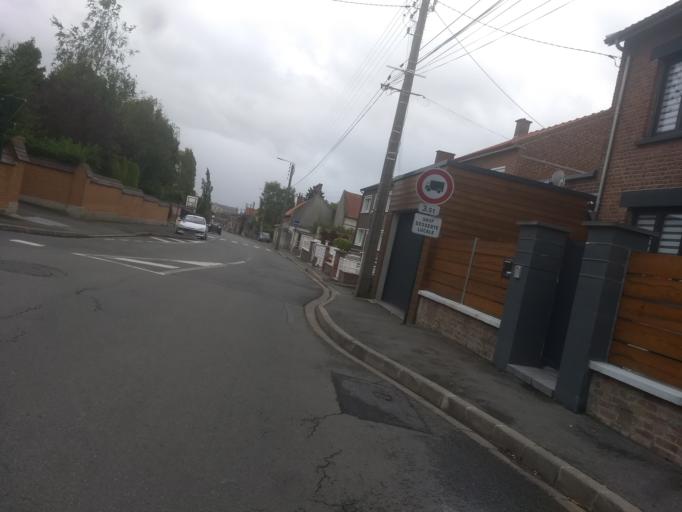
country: FR
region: Nord-Pas-de-Calais
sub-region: Departement du Pas-de-Calais
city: Saint-Nicolas
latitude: 50.3072
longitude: 2.7780
